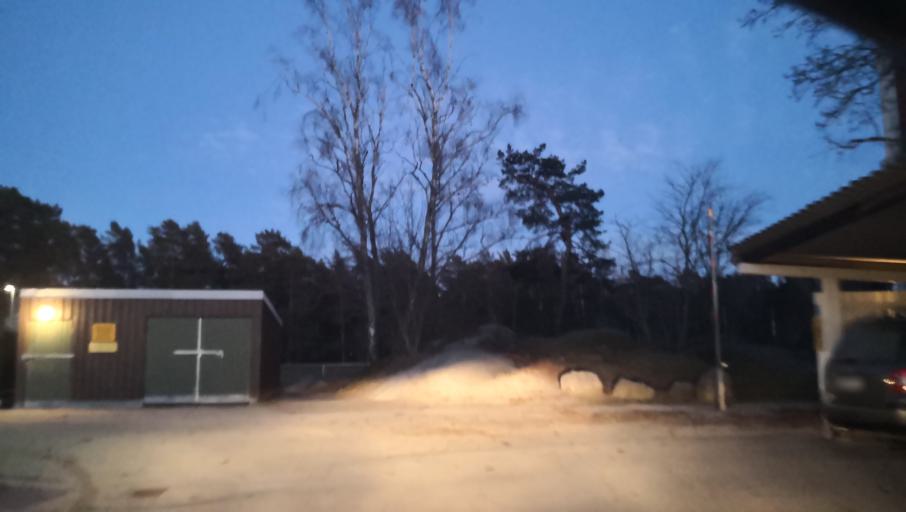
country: SE
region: Stockholm
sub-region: Nynashamns Kommun
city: Nynashamn
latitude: 58.9139
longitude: 17.9391
